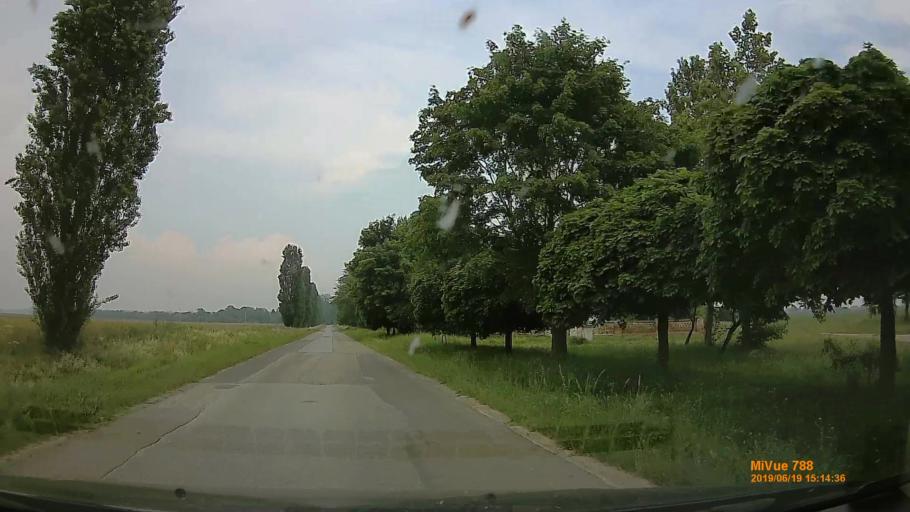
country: HU
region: Baranya
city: Szigetvar
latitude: 46.0693
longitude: 17.8263
